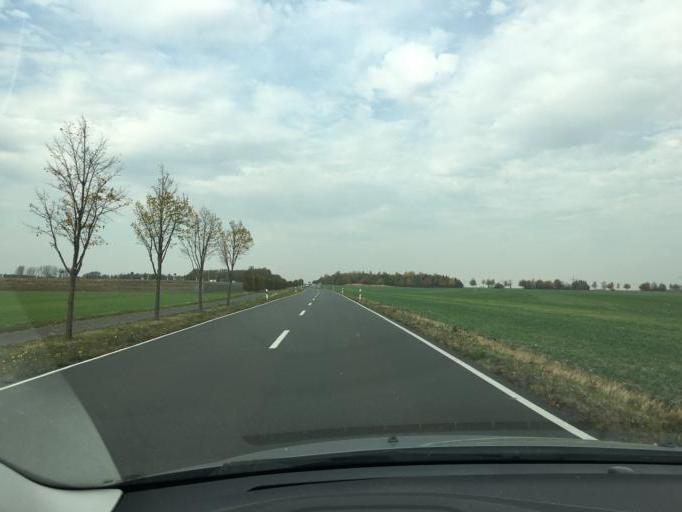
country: DE
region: Saxony
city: Zwochau
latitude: 51.4313
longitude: 12.2838
